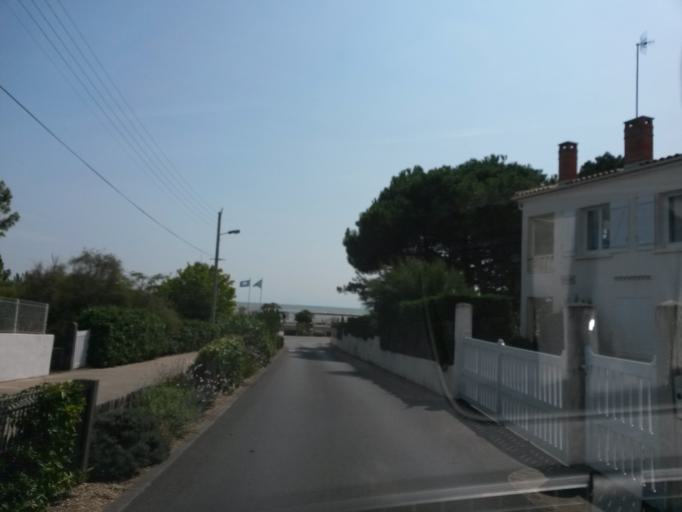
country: FR
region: Pays de la Loire
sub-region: Departement de la Vendee
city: La Tranche-sur-Mer
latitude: 46.3430
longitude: -1.4357
